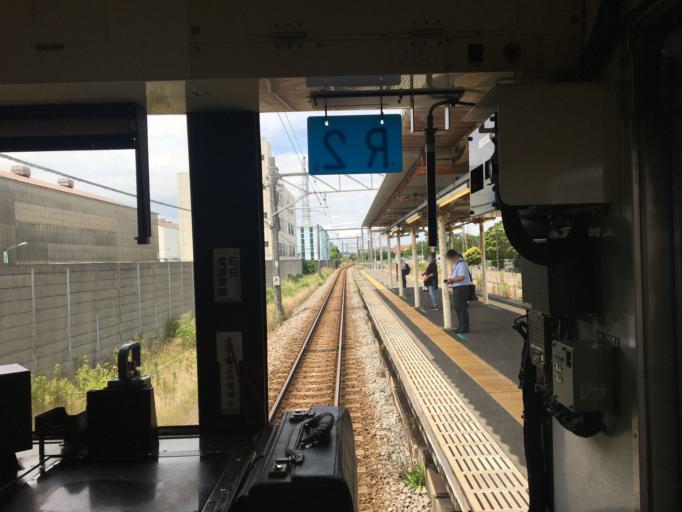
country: JP
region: Kanagawa
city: Chigasaki
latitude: 35.3395
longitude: 139.4074
